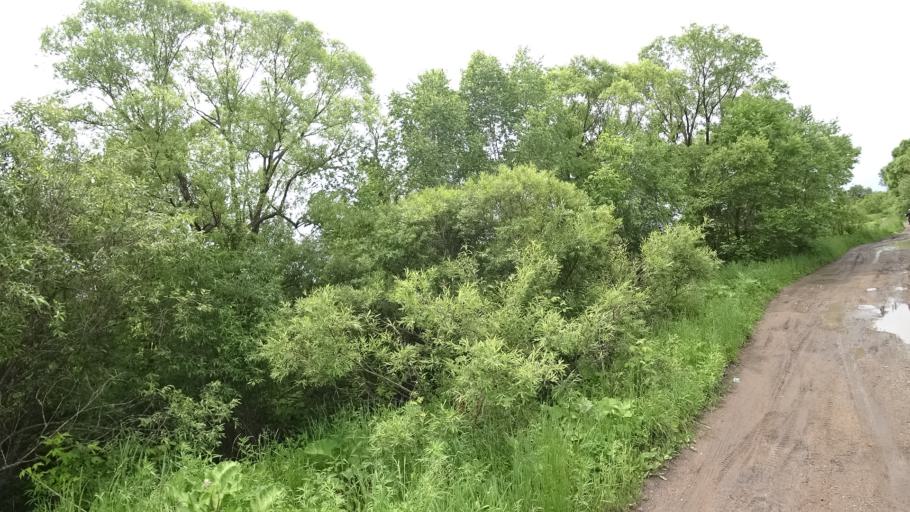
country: RU
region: Primorskiy
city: Novosysoyevka
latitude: 44.2282
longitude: 133.3724
